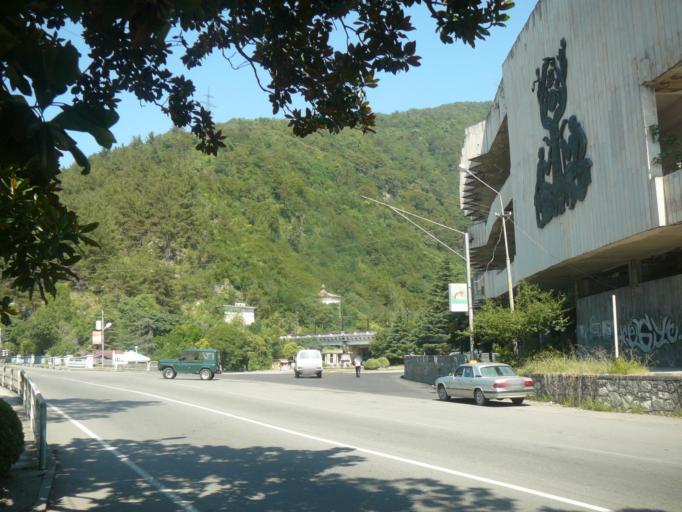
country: GE
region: Abkhazia
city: Gagra
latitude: 43.3257
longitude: 40.2241
